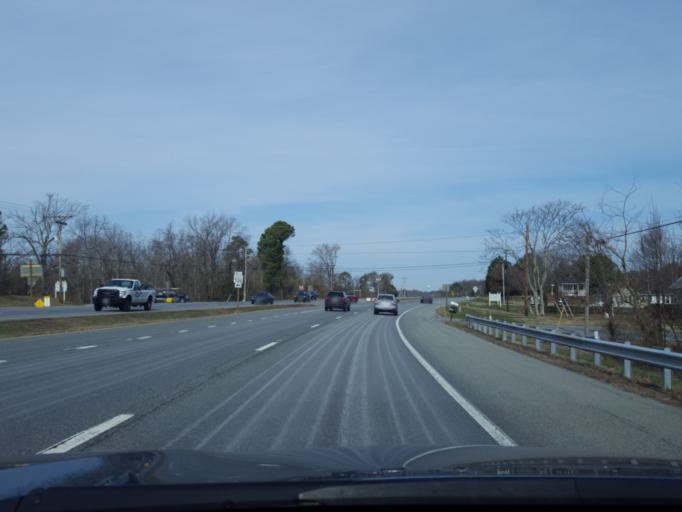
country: US
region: Maryland
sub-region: Calvert County
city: Prince Frederick
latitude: 38.5093
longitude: -76.5633
